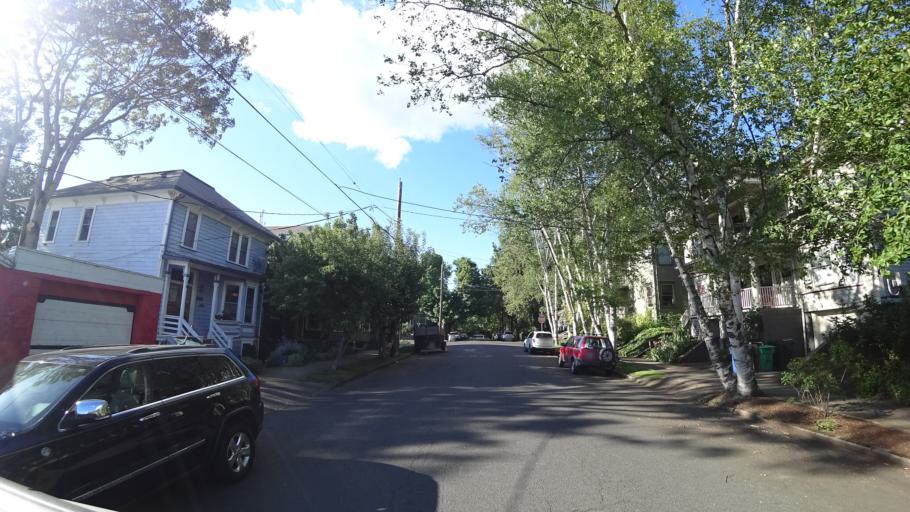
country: US
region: Oregon
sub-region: Multnomah County
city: Portland
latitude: 45.5175
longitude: -122.6496
